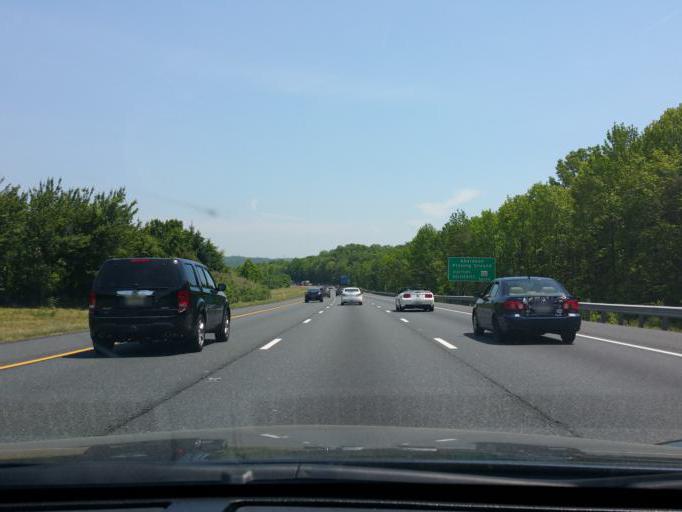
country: US
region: Maryland
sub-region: Harford County
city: Riverside
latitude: 39.4679
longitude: -76.2824
